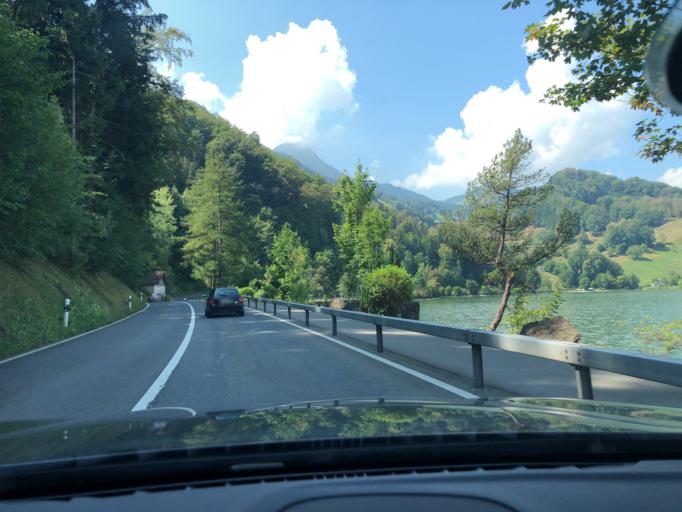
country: CH
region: Schwyz
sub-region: Bezirk Schwyz
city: Ingenbohl
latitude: 47.0269
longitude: 8.6133
